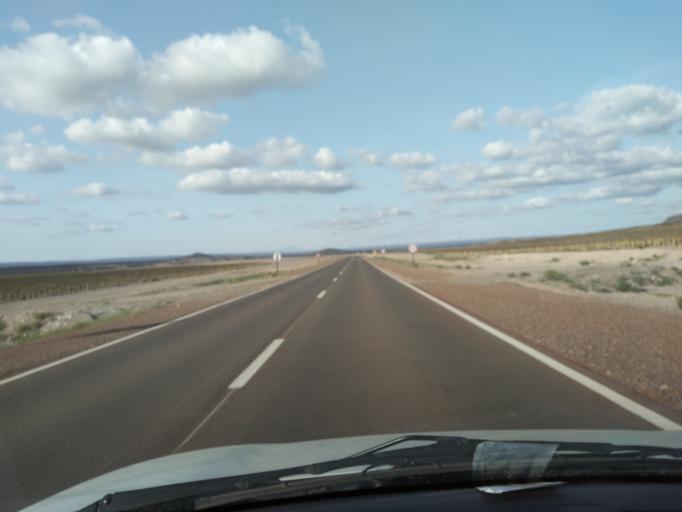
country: AR
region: Mendoza
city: San Rafael
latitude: -34.6531
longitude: -69.1579
